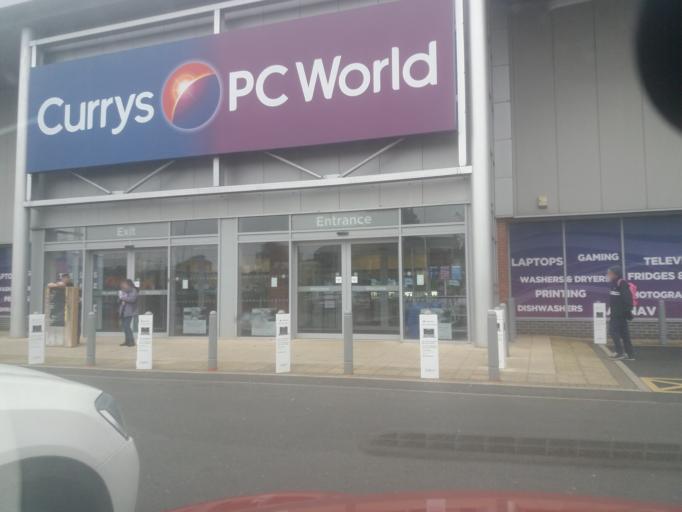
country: GB
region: England
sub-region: Lancashire
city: Chorley
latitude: 53.6604
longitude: -2.6278
